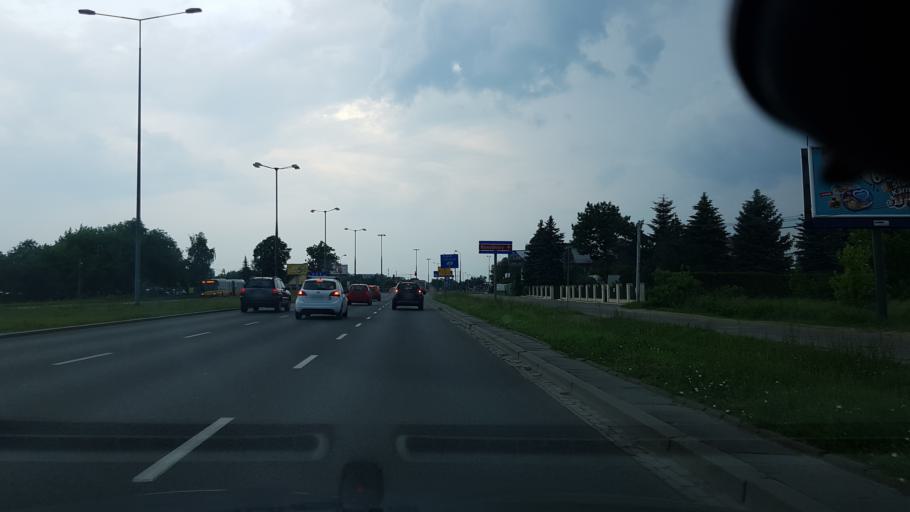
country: PL
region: Masovian Voivodeship
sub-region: Warszawa
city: Bialoleka
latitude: 52.3420
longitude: 20.9536
